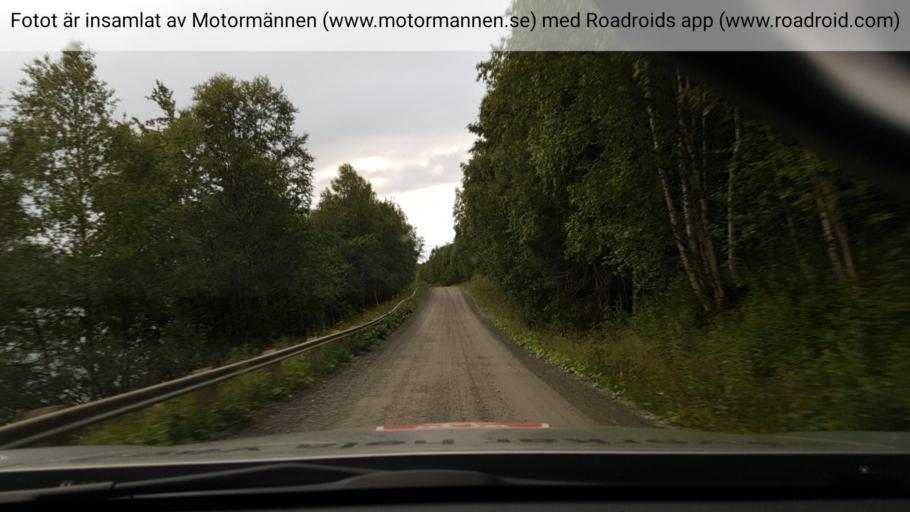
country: NO
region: Nordland
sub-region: Hattfjelldal
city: Hattfjelldal
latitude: 65.6478
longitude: 15.1830
